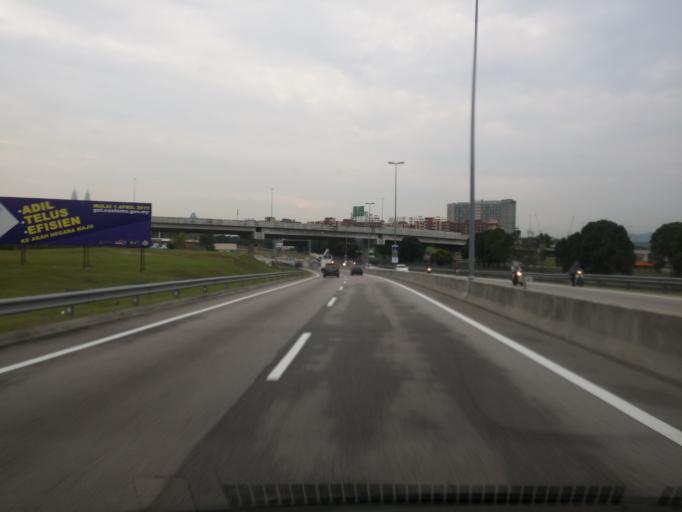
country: MY
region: Kuala Lumpur
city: Kuala Lumpur
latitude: 3.1166
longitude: 101.7161
